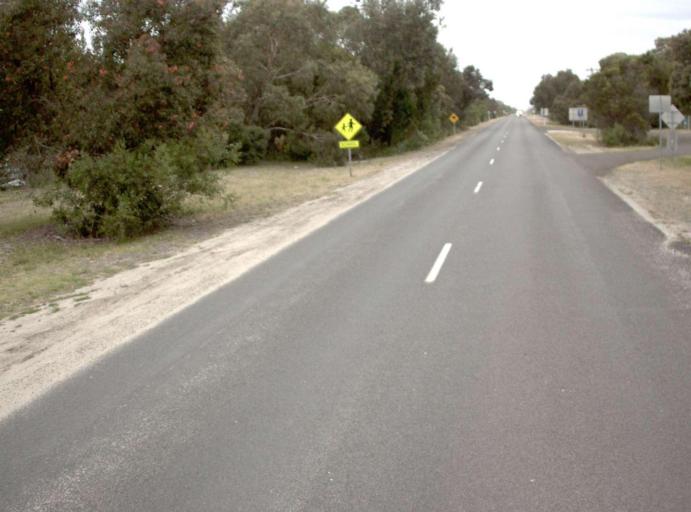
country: AU
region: Victoria
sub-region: East Gippsland
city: Bairnsdale
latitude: -38.0578
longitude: 147.5682
